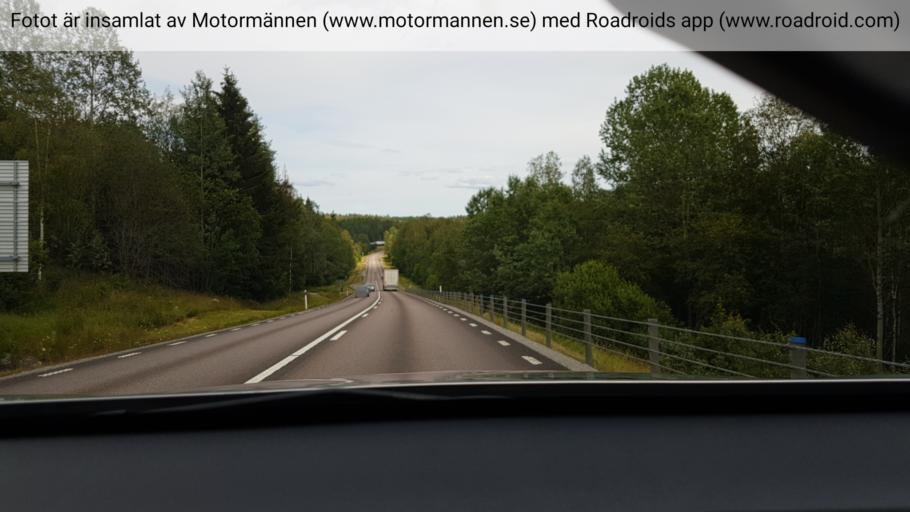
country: SE
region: Vaermland
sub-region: Sunne Kommun
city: Sunne
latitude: 59.6645
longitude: 12.8950
